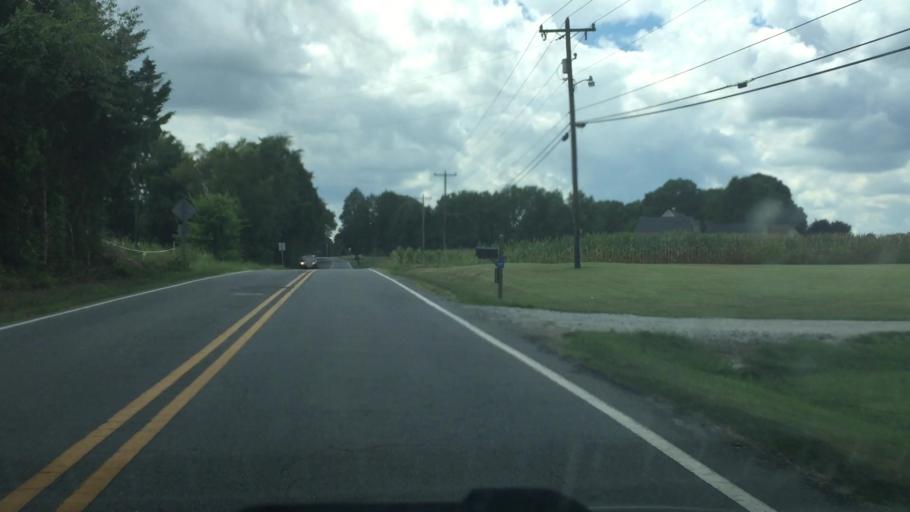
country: US
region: North Carolina
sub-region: Rowan County
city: Enochville
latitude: 35.4761
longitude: -80.7308
